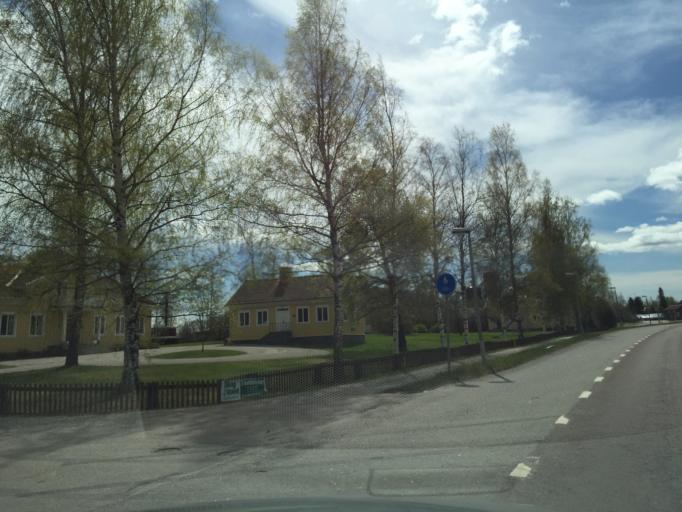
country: SE
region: Gaevleborg
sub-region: Bollnas Kommun
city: Arbra
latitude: 61.4893
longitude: 16.3739
